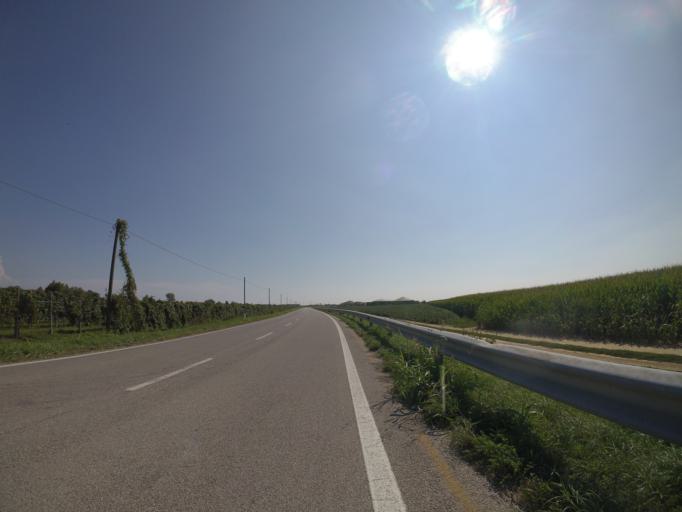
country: IT
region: Friuli Venezia Giulia
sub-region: Provincia di Udine
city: Carlino
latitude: 45.8005
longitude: 13.1657
